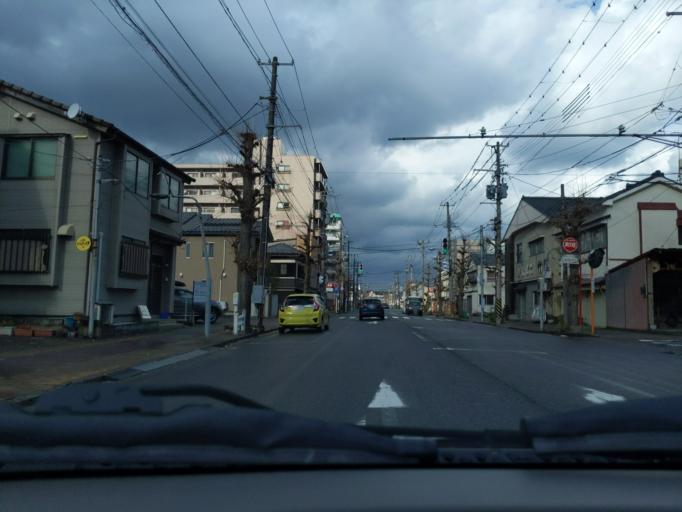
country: JP
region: Niigata
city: Niigata-shi
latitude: 37.9271
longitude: 139.0470
